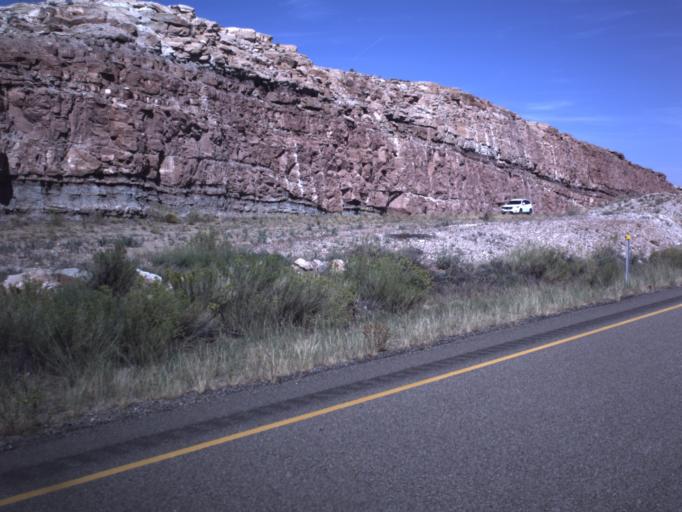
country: US
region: Utah
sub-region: Carbon County
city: East Carbon City
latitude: 38.9211
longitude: -110.3910
